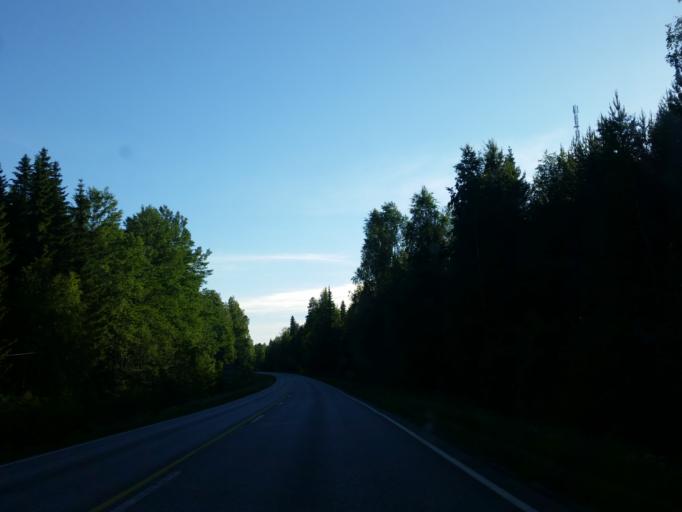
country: FI
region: Northern Savo
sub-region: Kuopio
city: Karttula
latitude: 62.8675
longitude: 27.1576
